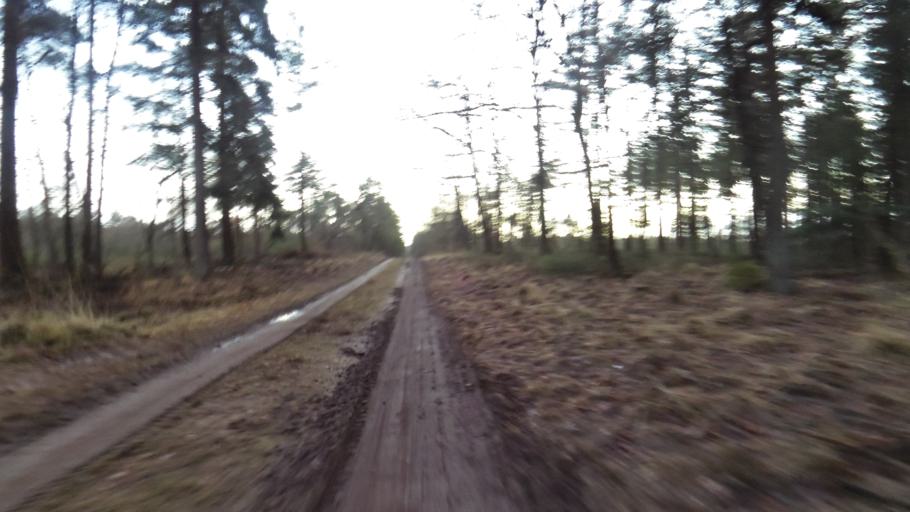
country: NL
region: Gelderland
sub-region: Gemeente Apeldoorn
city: Uddel
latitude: 52.2731
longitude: 5.8475
